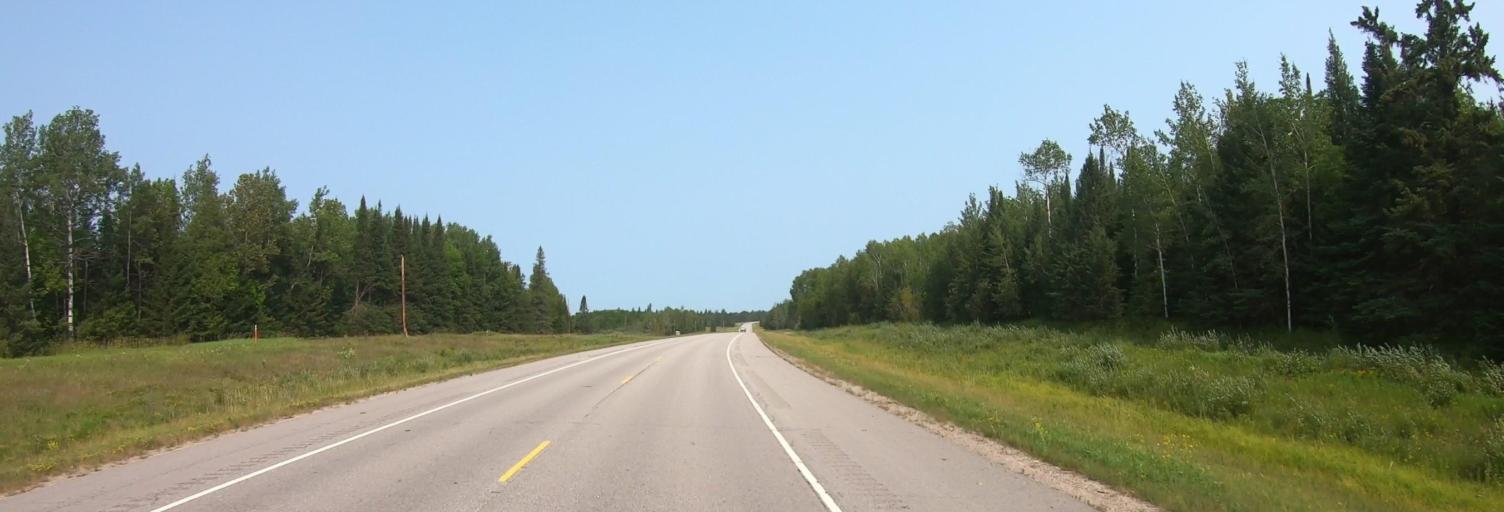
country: CA
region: Ontario
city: Fort Frances
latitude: 48.2861
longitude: -92.9684
